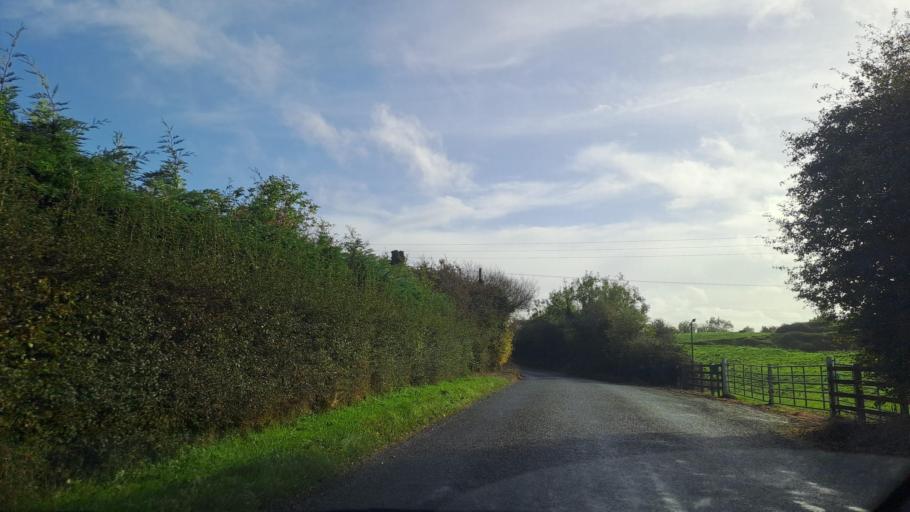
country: IE
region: Ulster
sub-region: County Monaghan
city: Carrickmacross
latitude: 53.8851
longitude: -6.6905
